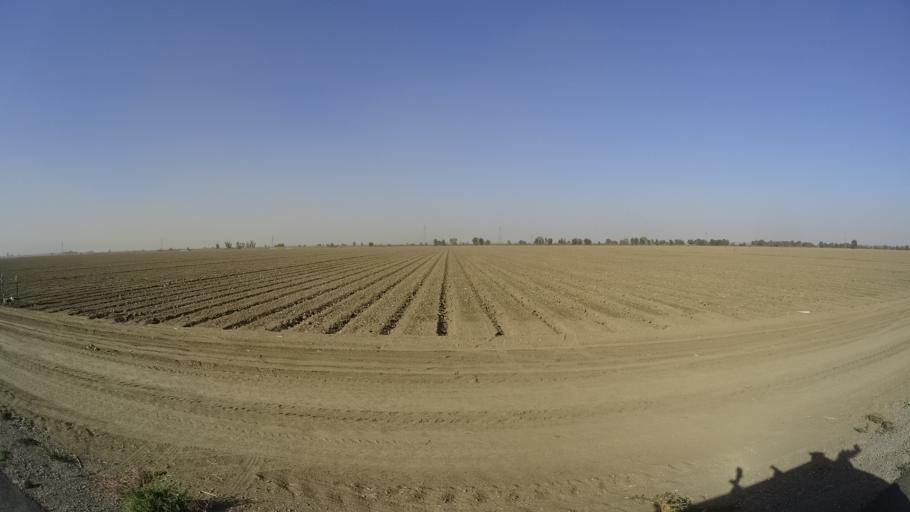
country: US
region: California
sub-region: Yolo County
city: Woodland
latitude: 38.7929
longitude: -121.7567
